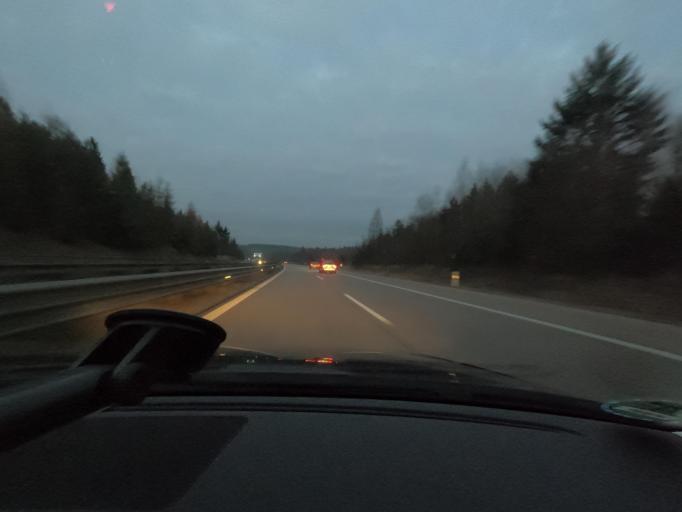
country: DE
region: Bavaria
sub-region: Upper Franconia
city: Lichtenfels
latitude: 50.2028
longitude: 11.0428
